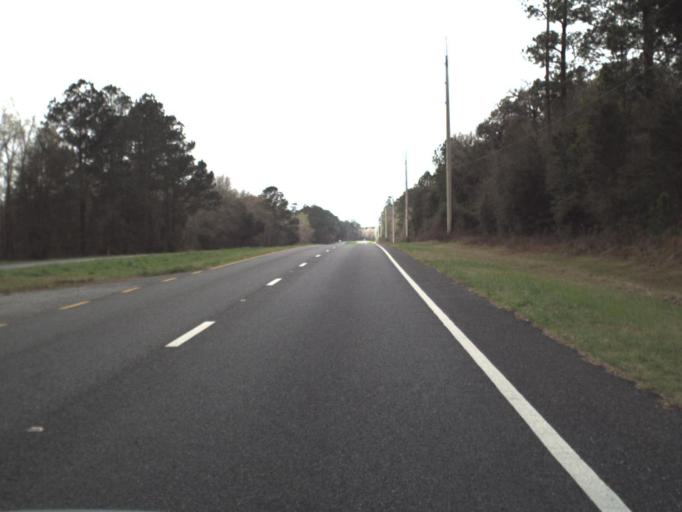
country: US
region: Florida
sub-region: Jefferson County
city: Monticello
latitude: 30.4033
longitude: -84.0368
